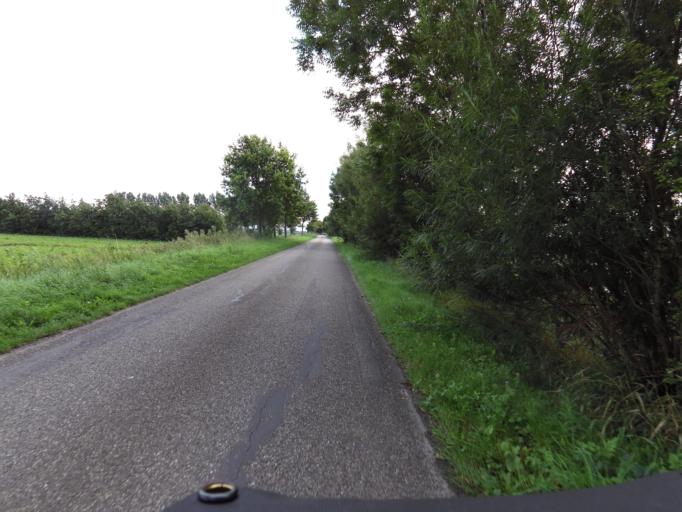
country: NL
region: South Holland
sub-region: Gemeente Goeree-Overflakkee
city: Middelharnis
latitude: 51.7244
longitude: 4.2421
